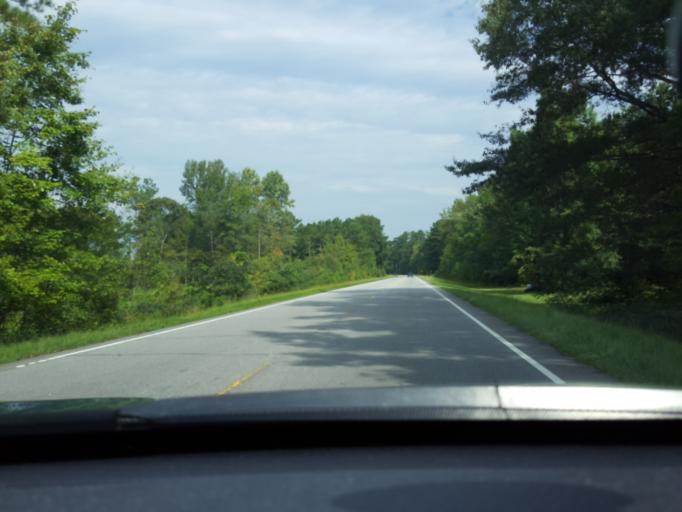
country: US
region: North Carolina
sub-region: Washington County
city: Plymouth
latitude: 35.9606
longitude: -76.7484
